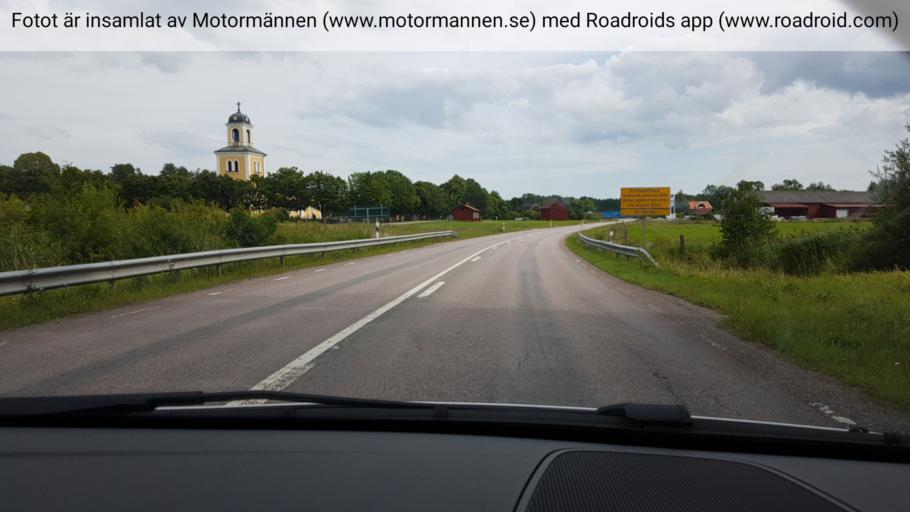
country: SE
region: Uppsala
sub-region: Osthammars Kommun
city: OEsthammar
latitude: 60.2431
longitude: 18.3399
